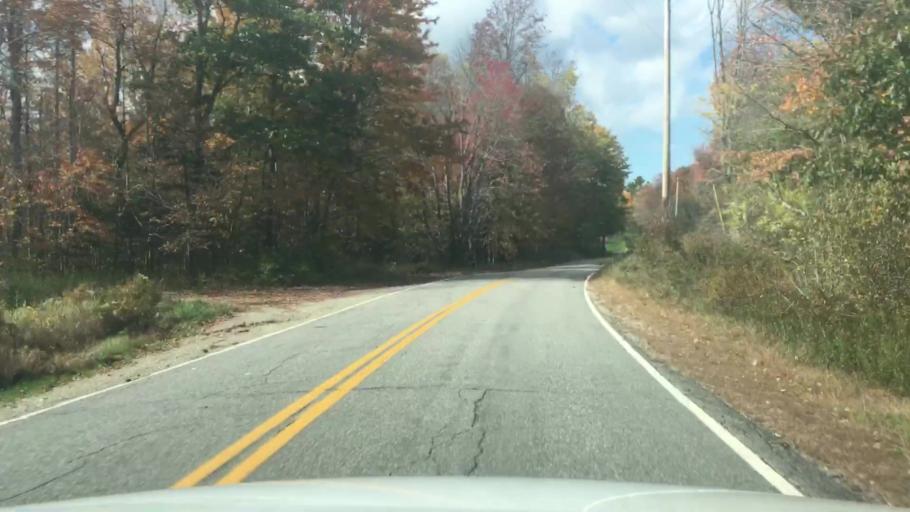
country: US
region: Maine
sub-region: Knox County
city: Washington
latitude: 44.3090
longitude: -69.3455
